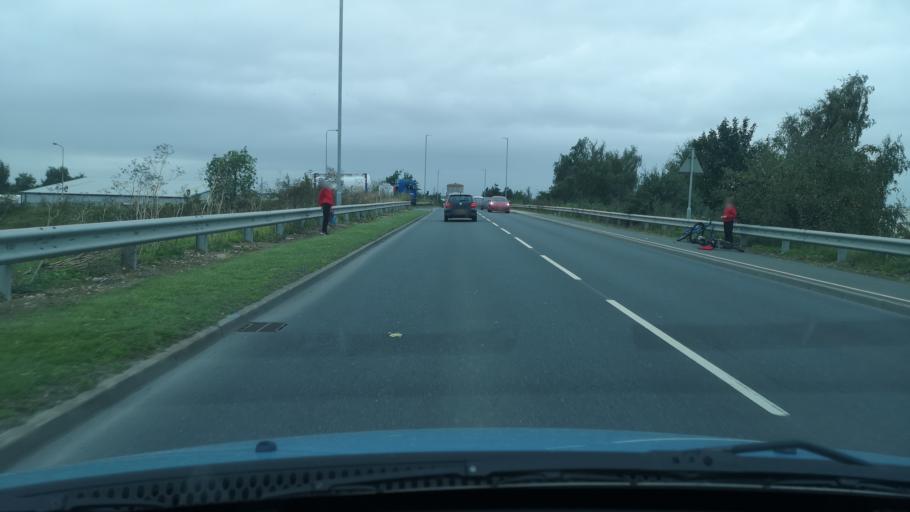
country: GB
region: England
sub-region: East Riding of Yorkshire
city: Goole
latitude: 53.6990
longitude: -0.8846
